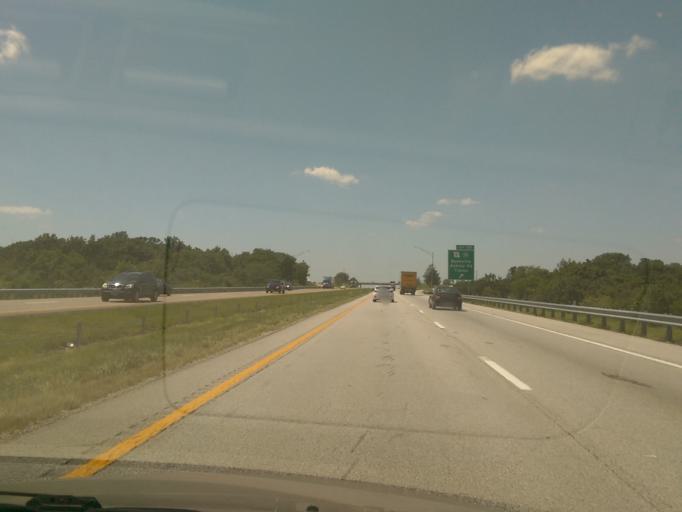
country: US
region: Missouri
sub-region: Cooper County
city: Boonville
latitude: 38.9360
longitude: -92.7689
